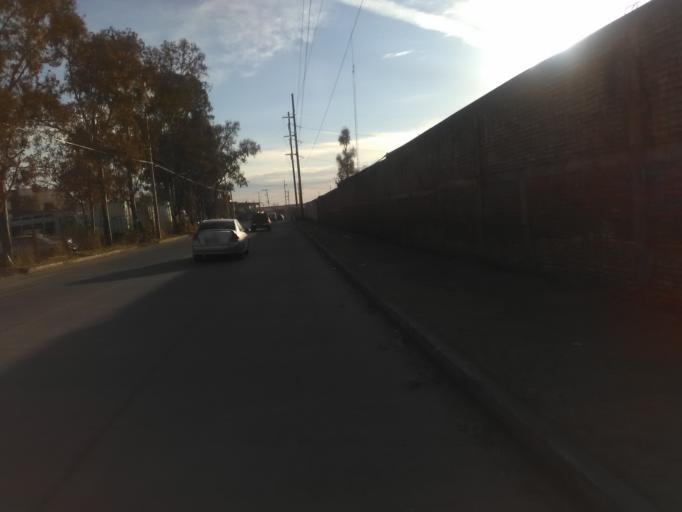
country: MX
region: Durango
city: Victoria de Durango
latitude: 24.0472
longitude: -104.6596
